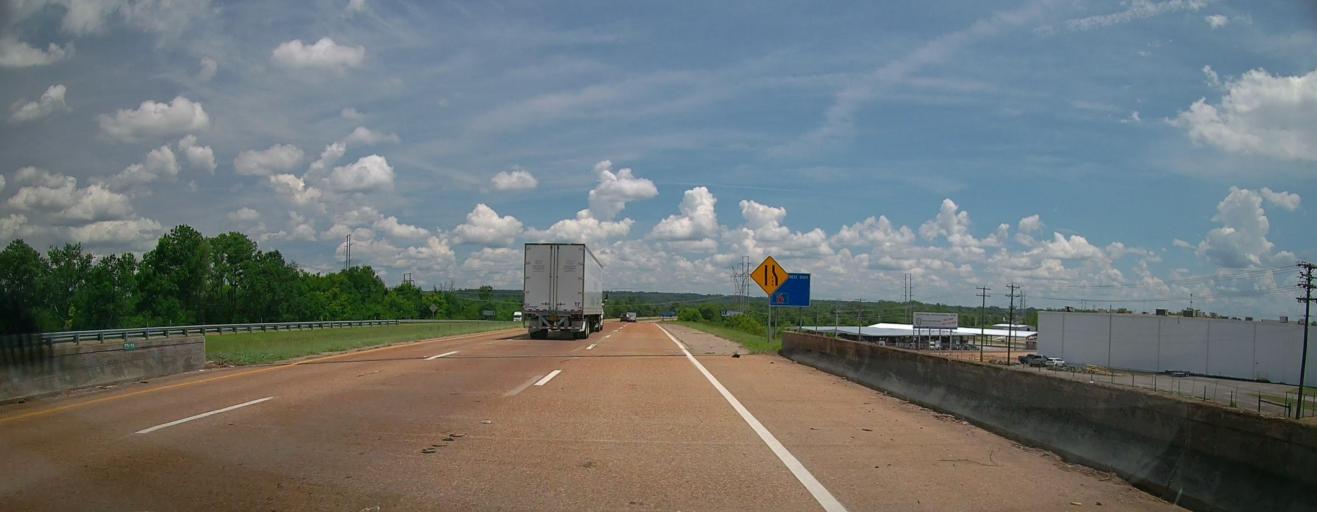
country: US
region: Mississippi
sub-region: Lee County
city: Tupelo
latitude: 34.2711
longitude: -88.7003
